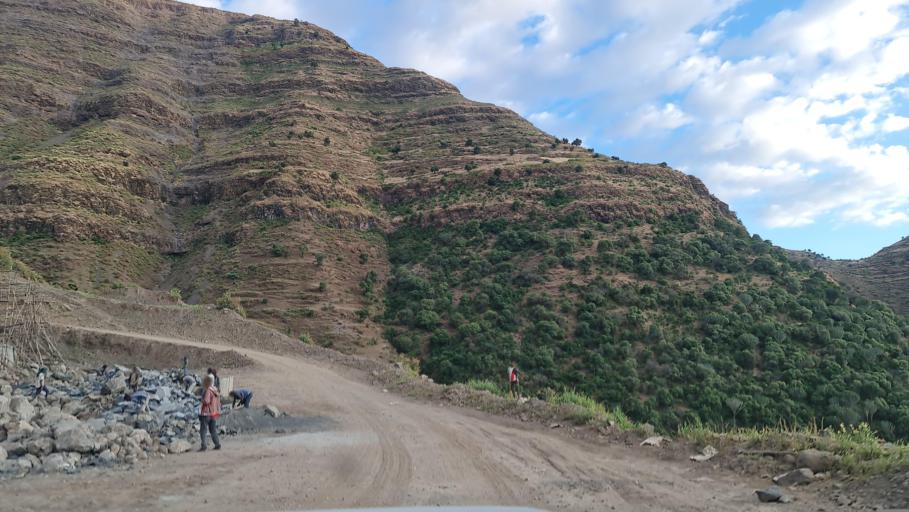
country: ET
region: Amhara
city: Debark'
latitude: 13.0112
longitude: 38.0467
